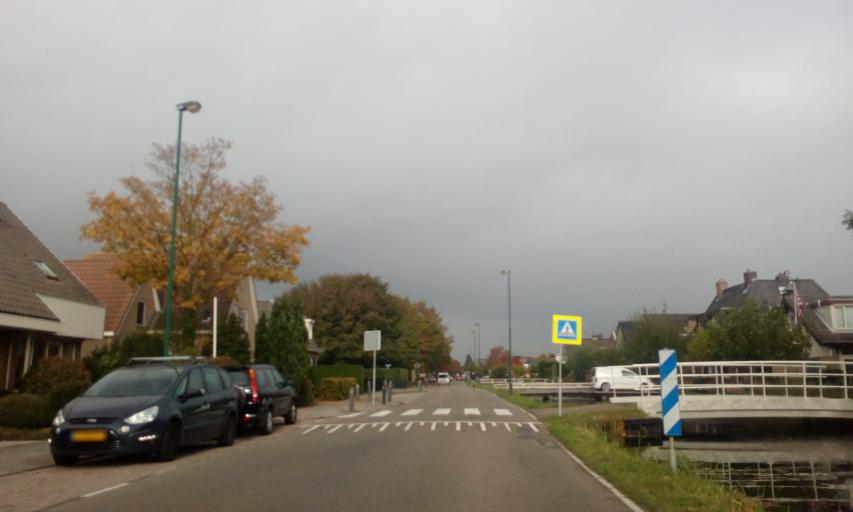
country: NL
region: South Holland
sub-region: Gemeente Lansingerland
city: Bergschenhoek
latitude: 51.9832
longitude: 4.4987
